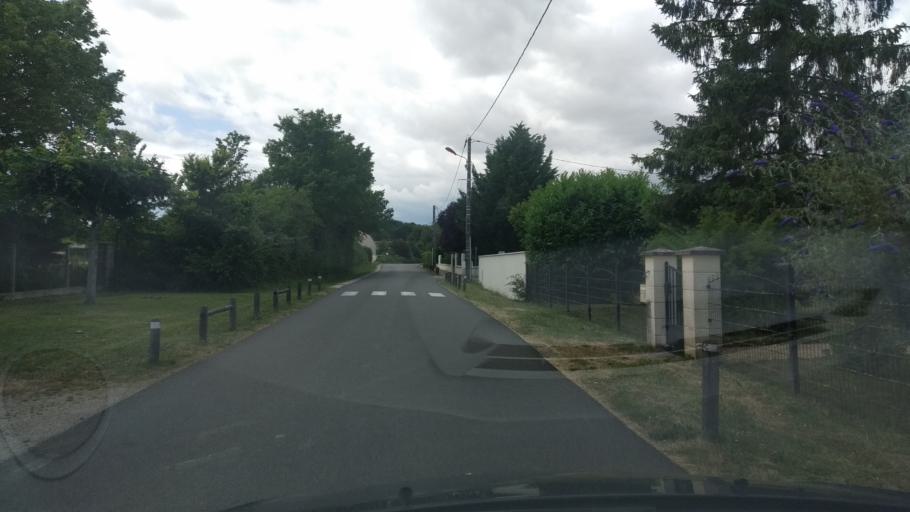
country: FR
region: Poitou-Charentes
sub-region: Departement de la Vienne
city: Cisse
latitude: 46.6201
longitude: 0.2093
